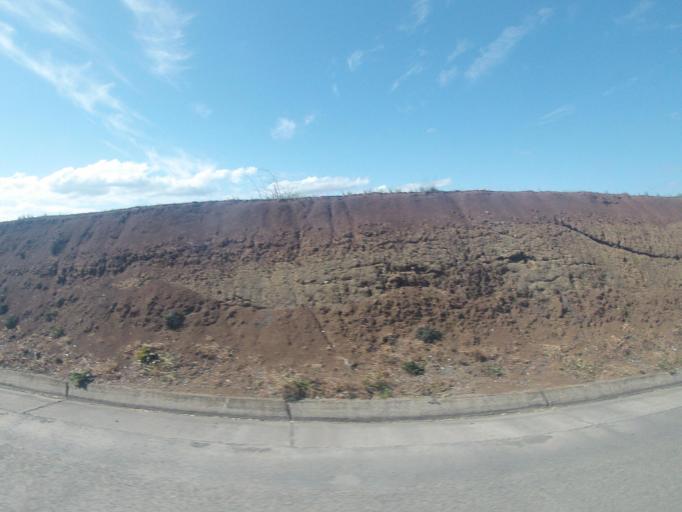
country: CL
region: Biobio
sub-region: Provincia de Biobio
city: Los Angeles
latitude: -37.4529
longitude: -72.4087
